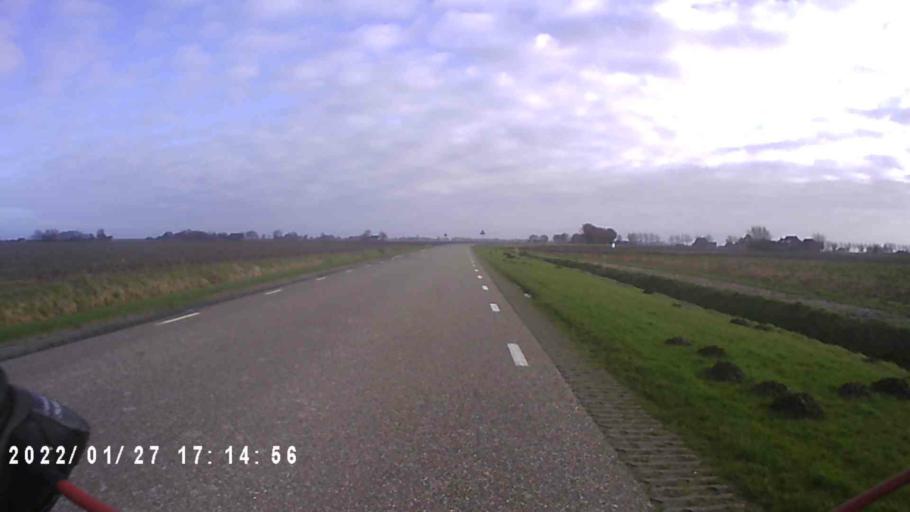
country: NL
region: Friesland
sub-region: Gemeente Dongeradeel
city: Anjum
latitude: 53.3946
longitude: 6.0961
